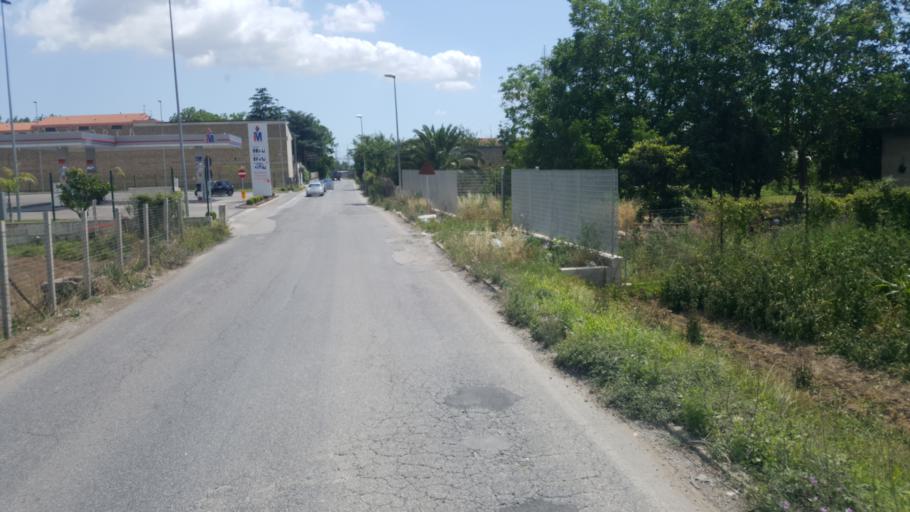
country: IT
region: Campania
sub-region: Provincia di Caserta
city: Maddaloni
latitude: 41.0229
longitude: 14.3743
